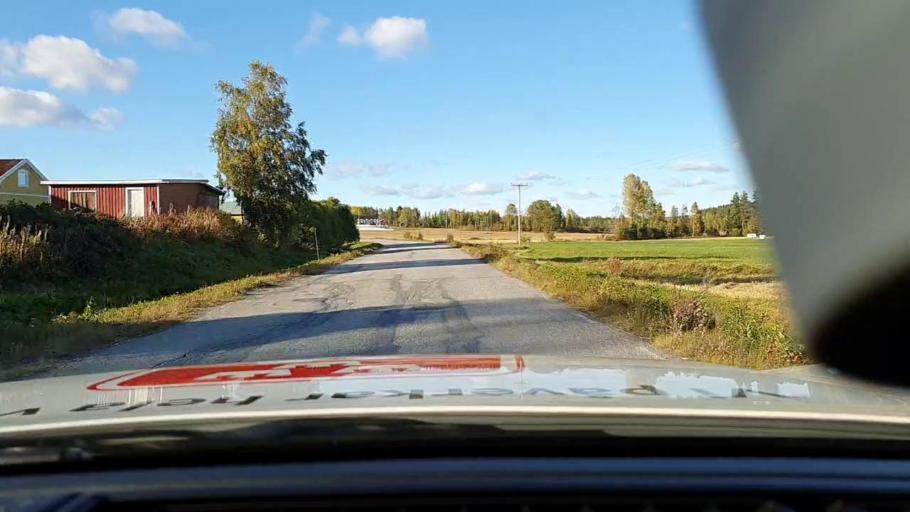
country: SE
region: Norrbotten
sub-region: Pitea Kommun
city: Norrfjarden
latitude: 65.5226
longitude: 21.4922
